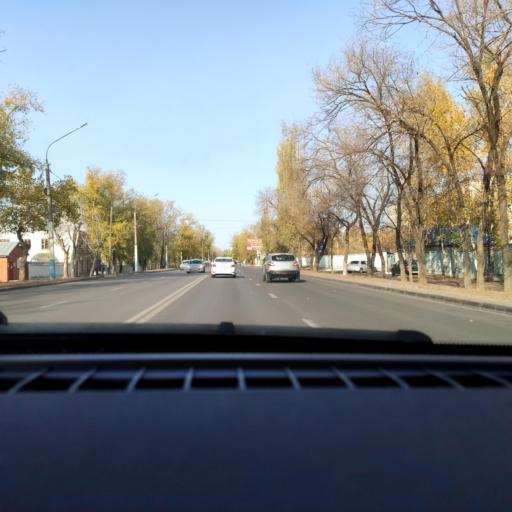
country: RU
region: Voronezj
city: Somovo
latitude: 51.7104
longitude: 39.2762
